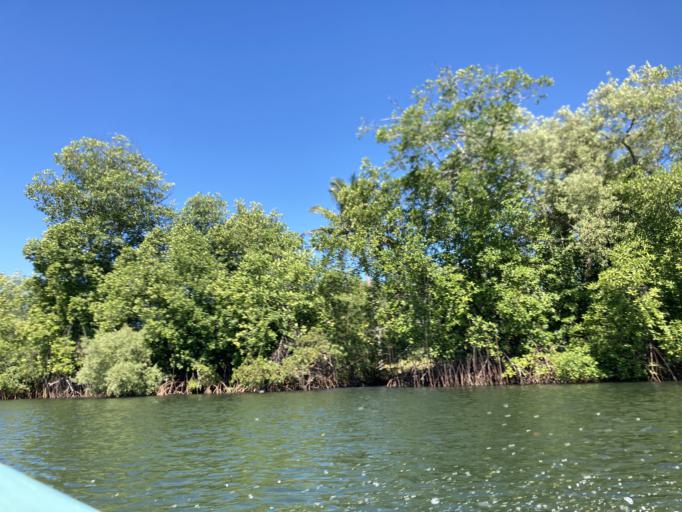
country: GT
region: Jutiapa
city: Pasaco
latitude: 13.8110
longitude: -90.2754
